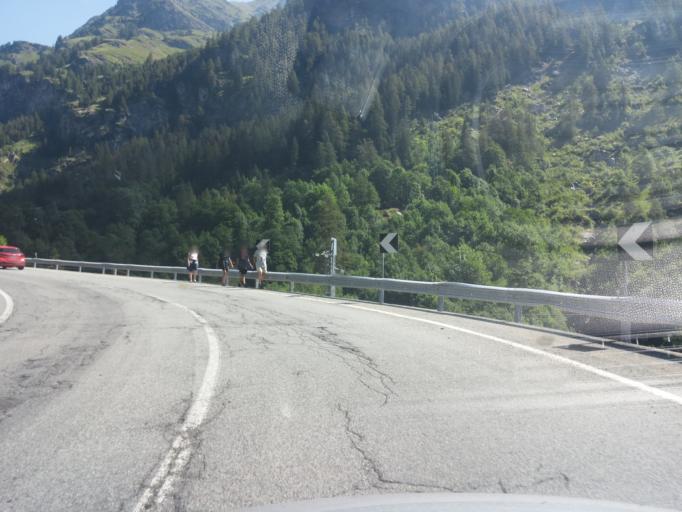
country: IT
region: Aosta Valley
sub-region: Valle d'Aosta
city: Gressoney-La-Trinite
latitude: 45.8069
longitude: 7.8243
